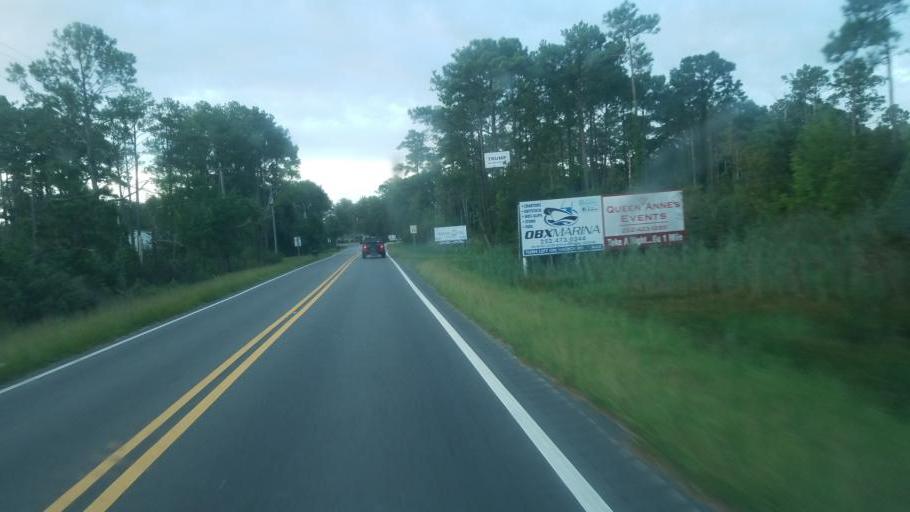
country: US
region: North Carolina
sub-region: Dare County
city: Wanchese
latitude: 35.8514
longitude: -75.6431
